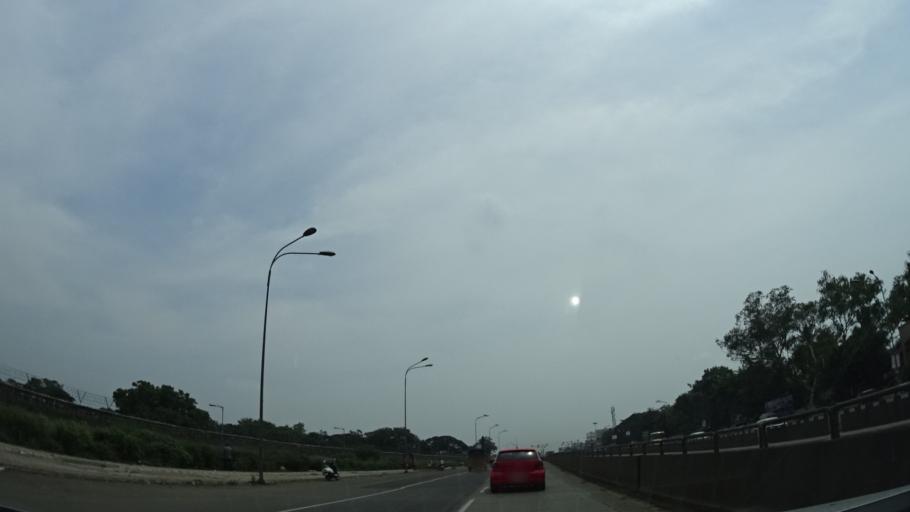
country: IN
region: Maharashtra
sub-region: Pune Division
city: Lohogaon
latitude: 18.5627
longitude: 73.9252
